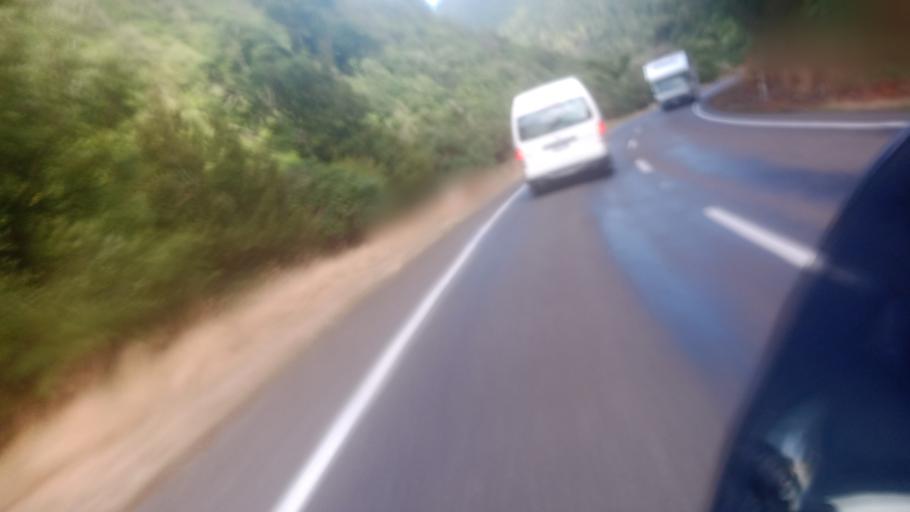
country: NZ
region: Bay of Plenty
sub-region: Opotiki District
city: Opotiki
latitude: -38.3228
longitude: 177.4018
